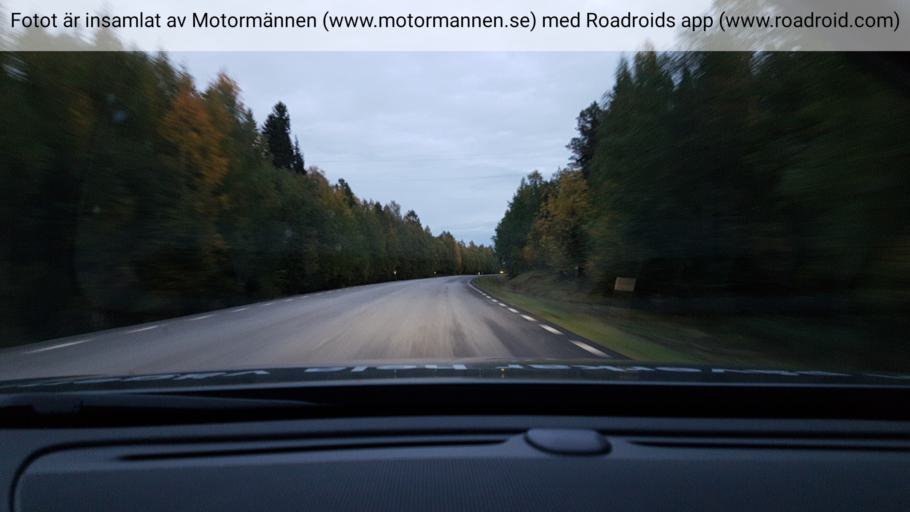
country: SE
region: Norrbotten
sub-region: Alvsbyns Kommun
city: AElvsbyn
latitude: 65.7841
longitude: 20.7553
